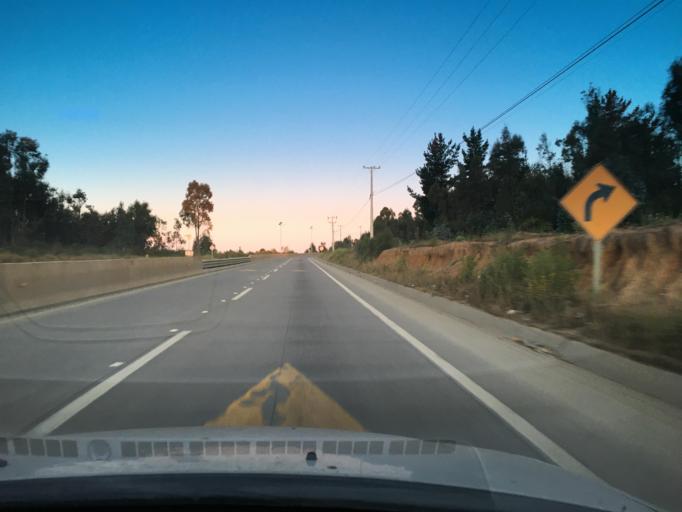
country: CL
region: Valparaiso
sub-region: Provincia de Valparaiso
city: Valparaiso
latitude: -33.0949
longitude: -71.5971
